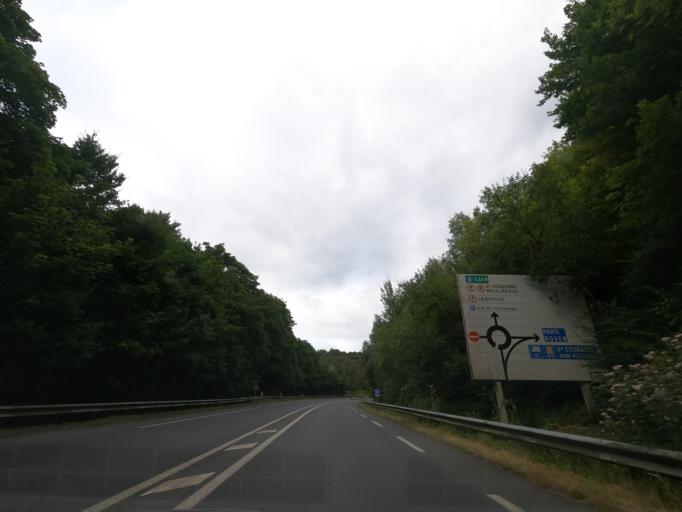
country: FR
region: Haute-Normandie
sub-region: Departement de la Seine-Maritime
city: Sahurs
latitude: 49.3378
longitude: 0.9205
